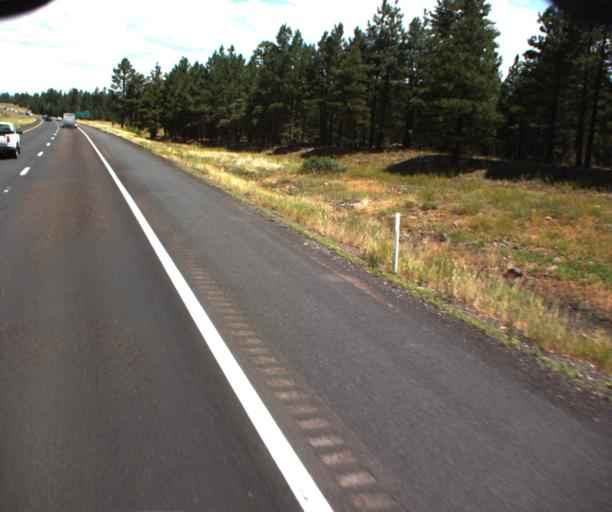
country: US
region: Arizona
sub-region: Coconino County
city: Sedona
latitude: 34.8925
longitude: -111.6414
